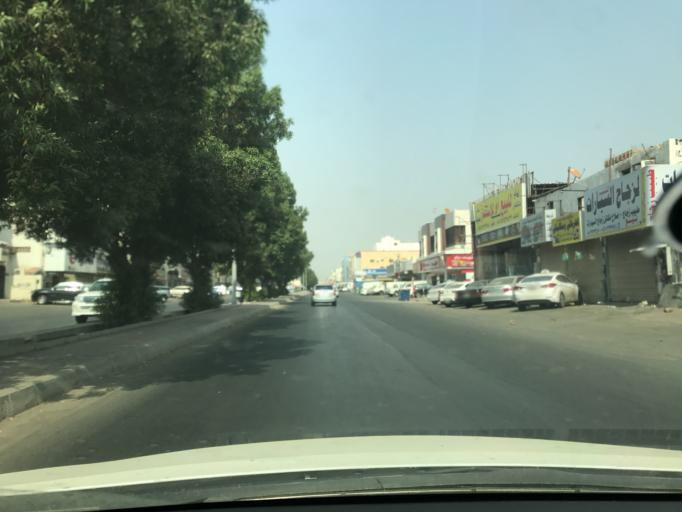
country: SA
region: Makkah
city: Jeddah
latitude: 21.6207
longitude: 39.1701
